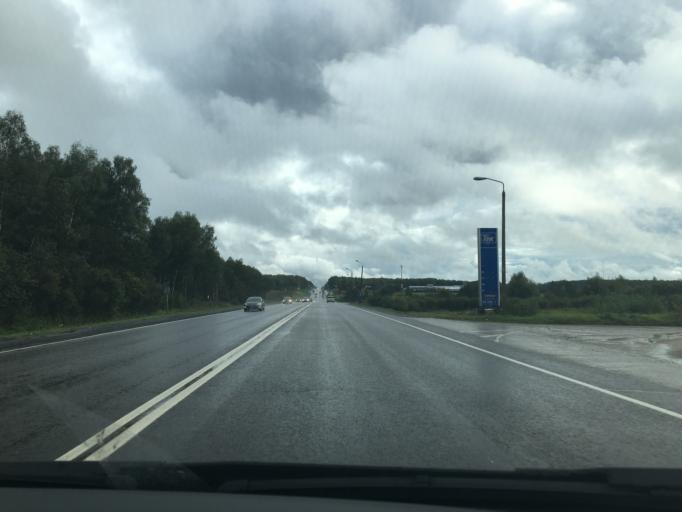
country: RU
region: Kaluga
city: Balabanovo
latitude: 55.1556
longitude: 36.6646
